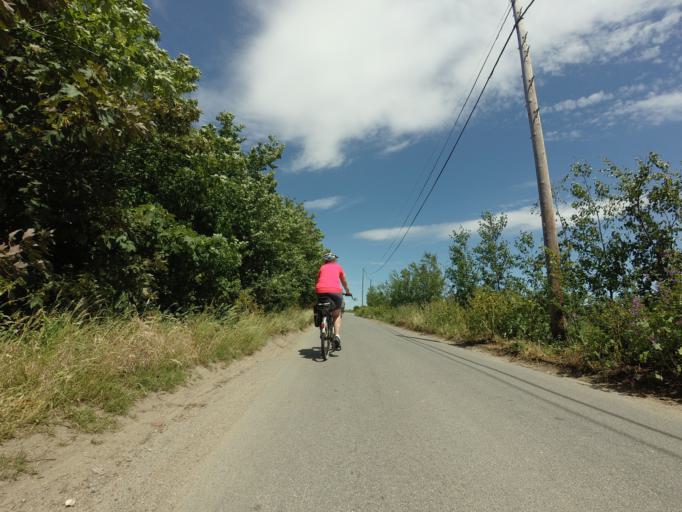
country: GB
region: England
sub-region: Kent
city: Cliffe
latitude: 51.4530
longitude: 0.4904
